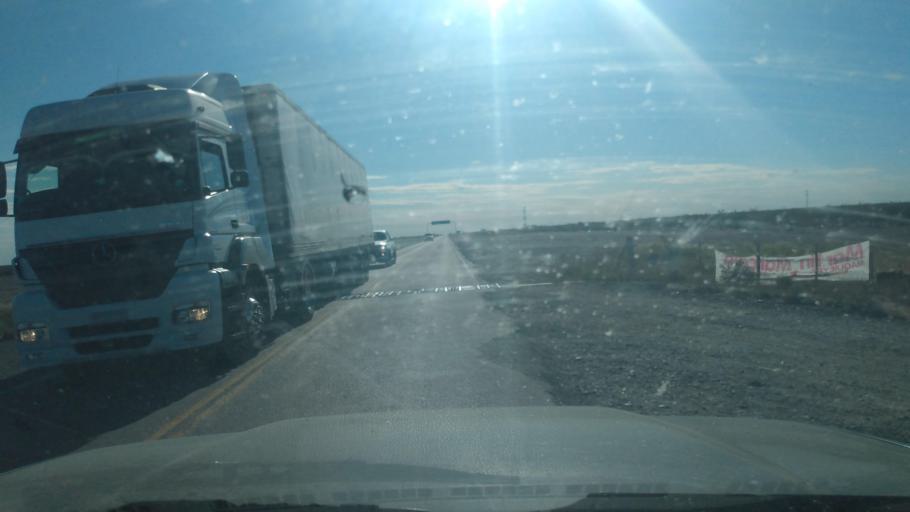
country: AR
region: La Pampa
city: Veinticinco de Mayo
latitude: -37.6603
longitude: -67.7480
